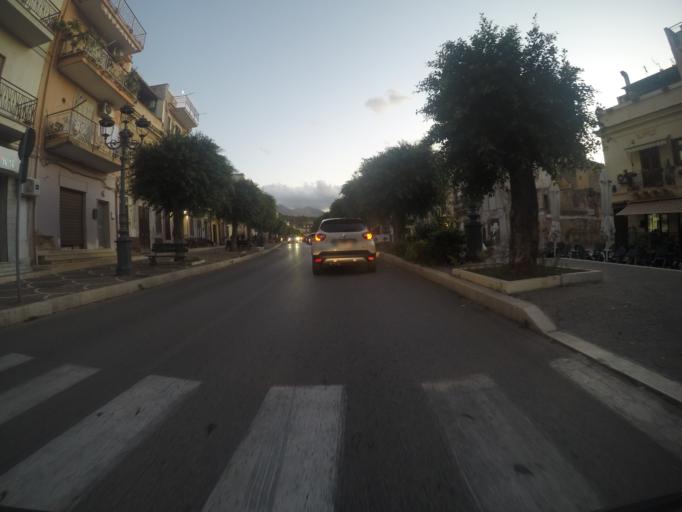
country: IT
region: Sicily
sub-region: Palermo
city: Capaci
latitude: 38.1733
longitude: 13.2405
